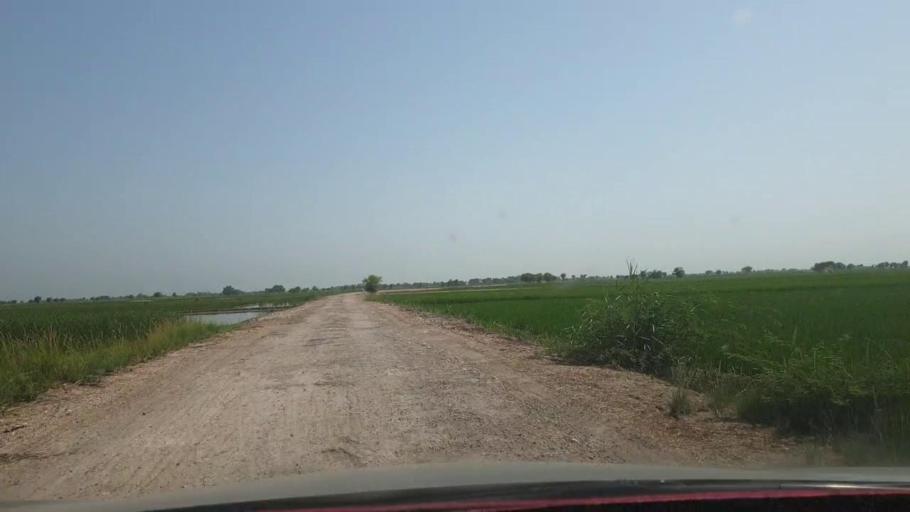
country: PK
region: Sindh
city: Nasirabad
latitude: 27.3691
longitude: 67.8530
